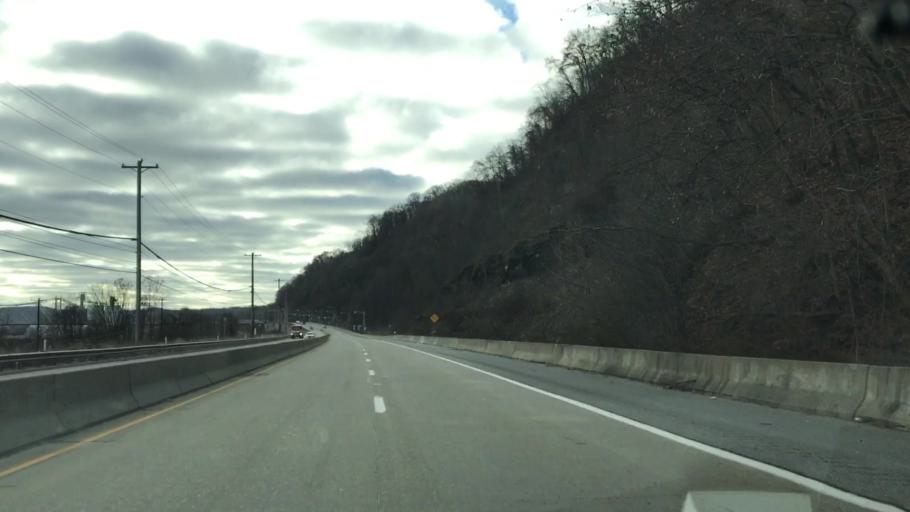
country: US
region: Pennsylvania
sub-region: Beaver County
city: Economy
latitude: 40.5980
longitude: -80.2419
